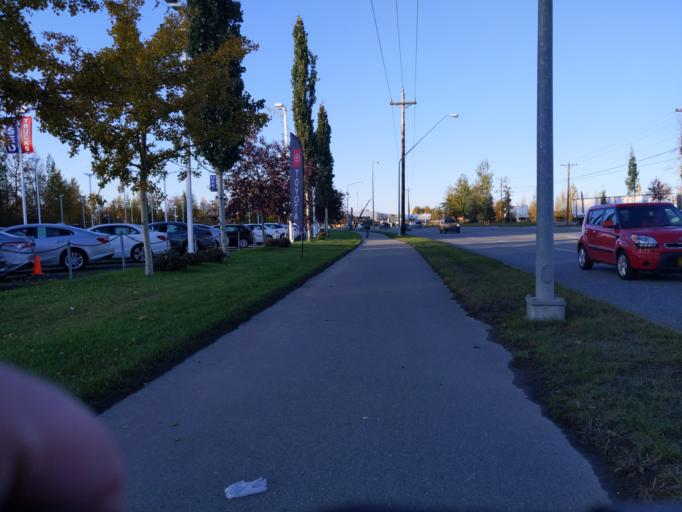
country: US
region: Alaska
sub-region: Anchorage Municipality
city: Anchorage
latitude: 61.1611
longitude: -149.8643
